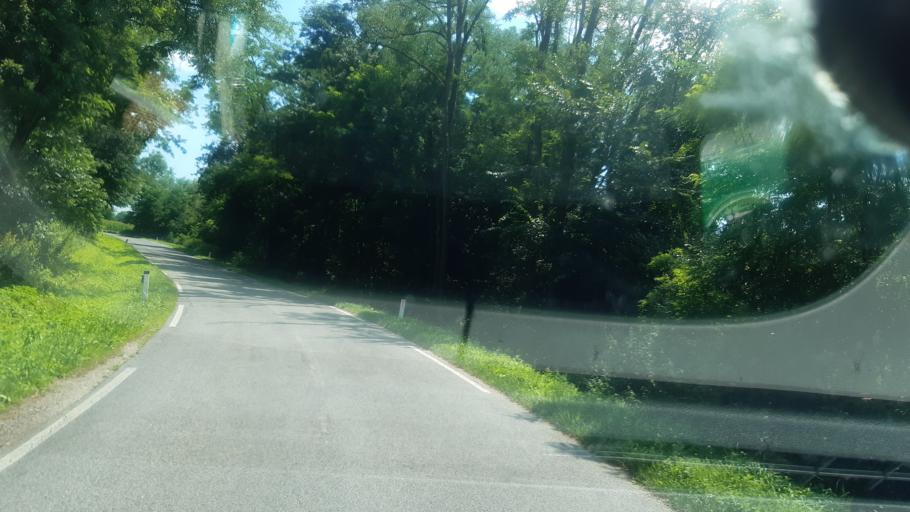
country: SI
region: Moravske Toplice
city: Moravske Toplice
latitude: 46.6644
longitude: 16.2321
